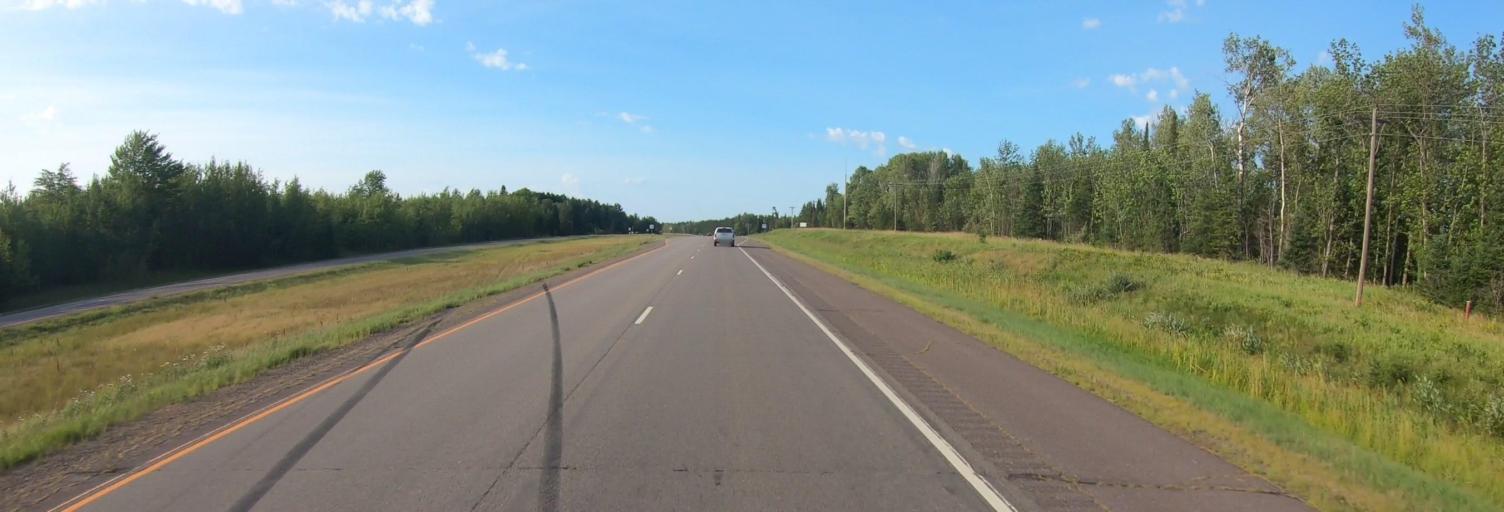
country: US
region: Minnesota
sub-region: Saint Louis County
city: Eveleth
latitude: 47.1238
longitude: -92.4721
